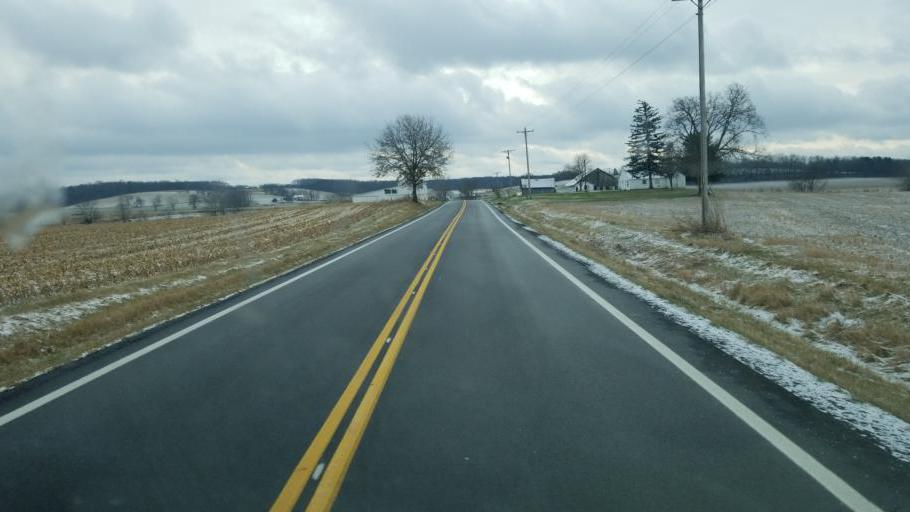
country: US
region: Ohio
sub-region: Knox County
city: Gambier
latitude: 40.3098
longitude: -82.3974
